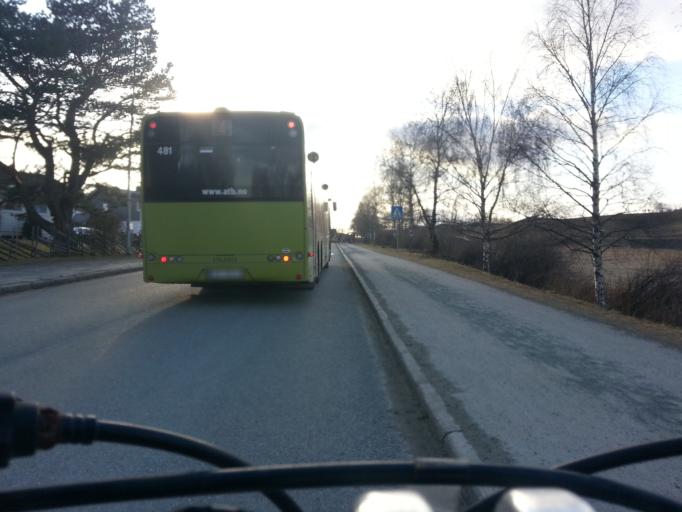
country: NO
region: Sor-Trondelag
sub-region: Trondheim
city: Trondheim
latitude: 63.4500
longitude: 10.4516
